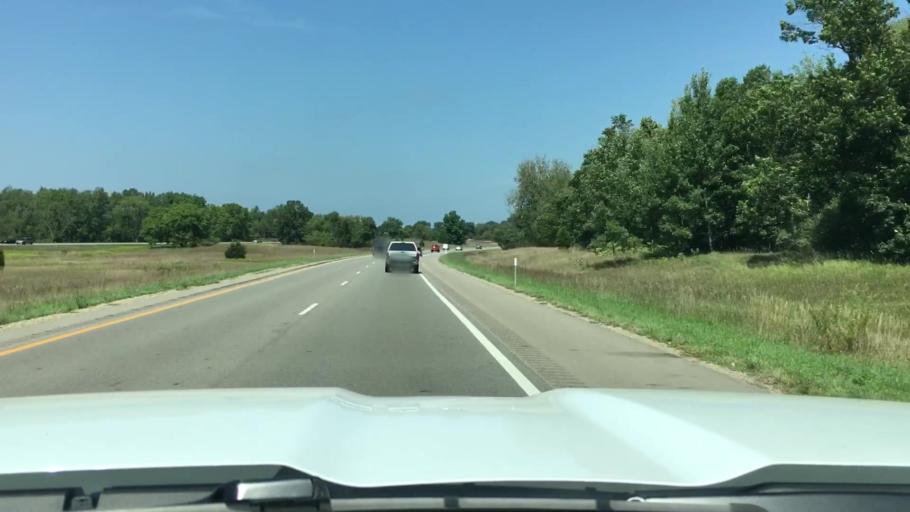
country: US
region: Michigan
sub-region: Kalamazoo County
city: Schoolcraft
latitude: 42.1536
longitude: -85.6421
